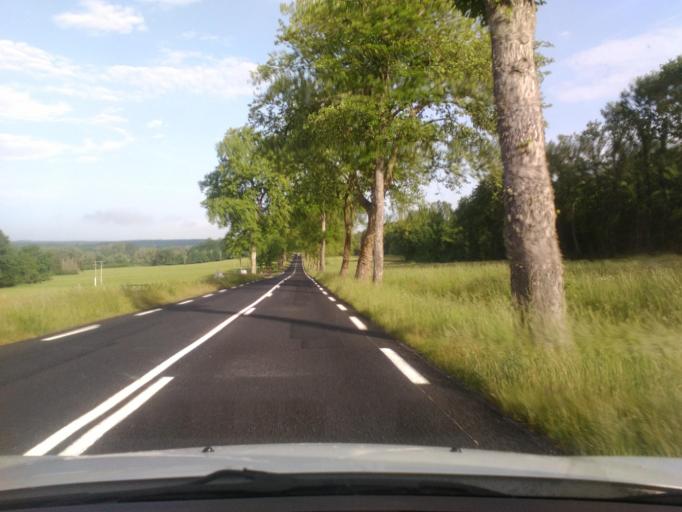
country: FR
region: Lorraine
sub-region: Departement de Meurthe-et-Moselle
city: Gerbeviller
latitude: 48.5170
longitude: 6.4857
